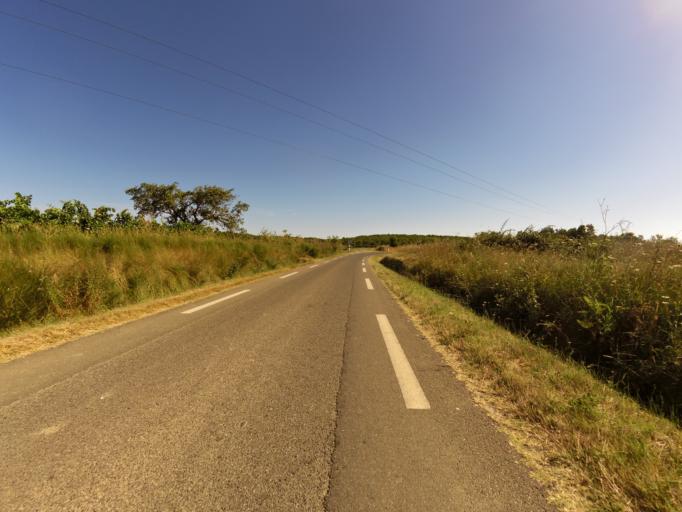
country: FR
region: Languedoc-Roussillon
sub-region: Departement du Gard
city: Aigues-Vives
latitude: 43.7483
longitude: 4.1841
